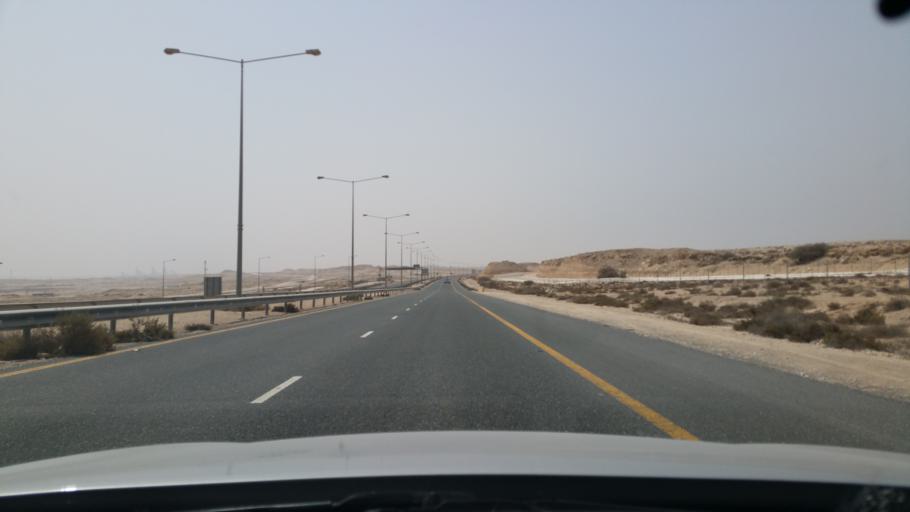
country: QA
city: Umm Bab
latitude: 25.2792
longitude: 50.7917
